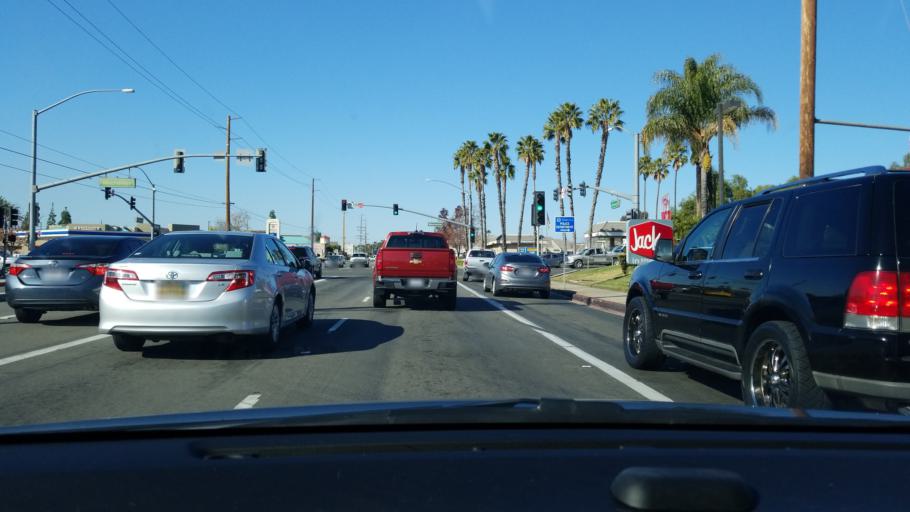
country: US
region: California
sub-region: Riverside County
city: Temecula
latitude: 33.5205
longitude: -117.1646
